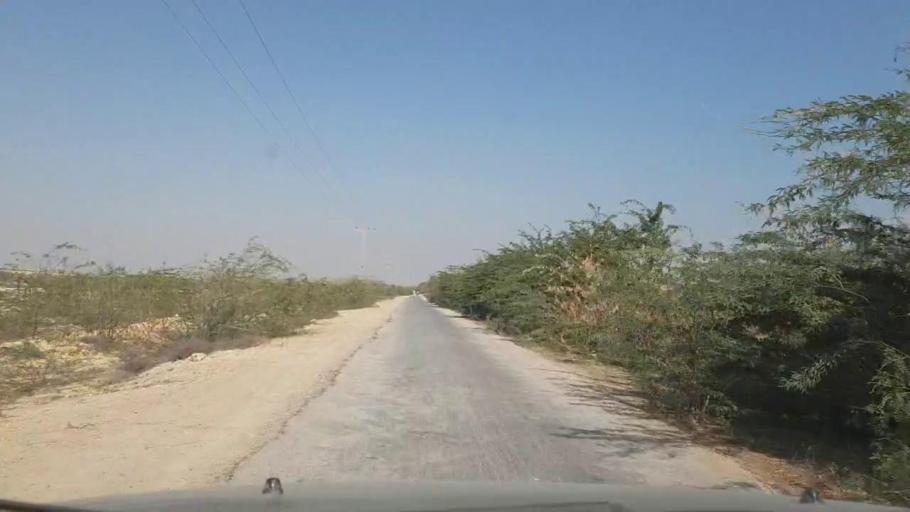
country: PK
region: Sindh
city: Daro Mehar
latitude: 25.0002
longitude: 68.0120
